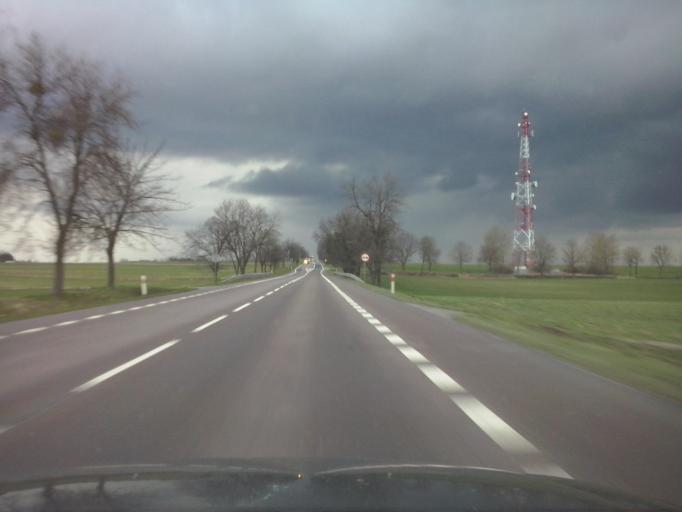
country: PL
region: Lublin Voivodeship
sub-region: Powiat chelmski
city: Rejowiec Fabryczny
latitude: 51.1774
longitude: 23.2252
